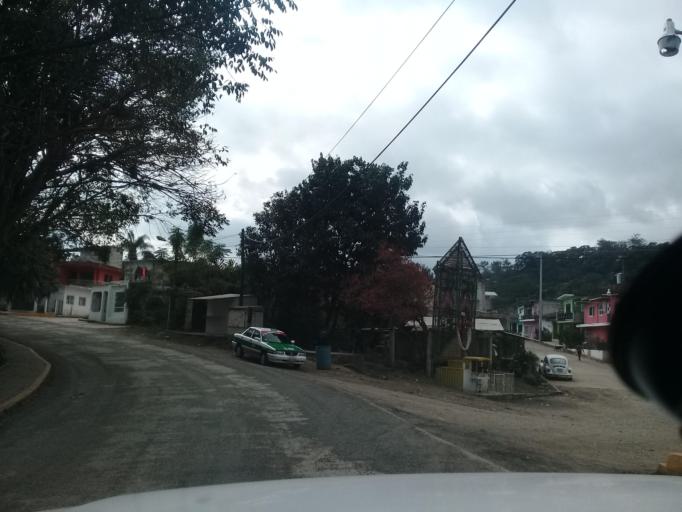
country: MX
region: Veracruz
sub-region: Xalapa
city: Fraccionamiento las Fuentes
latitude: 19.4738
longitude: -96.8814
